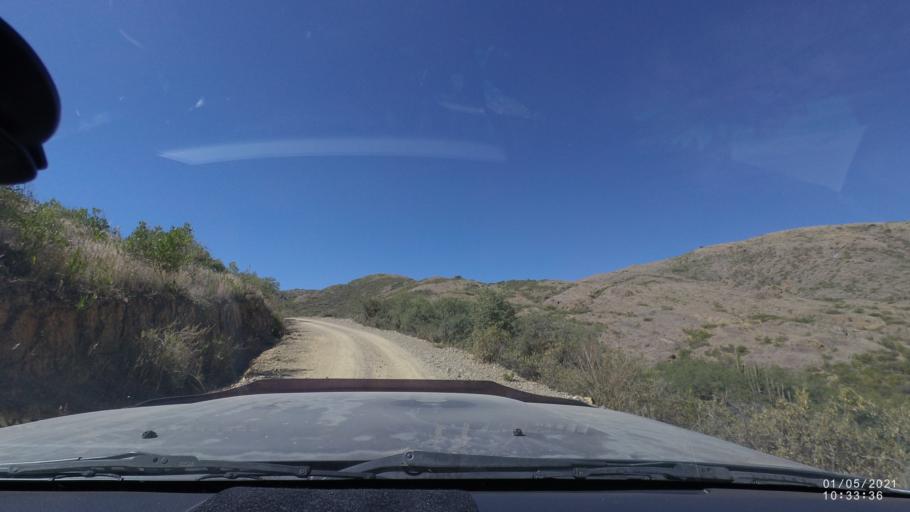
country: BO
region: Cochabamba
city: Capinota
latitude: -17.5975
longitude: -66.1938
